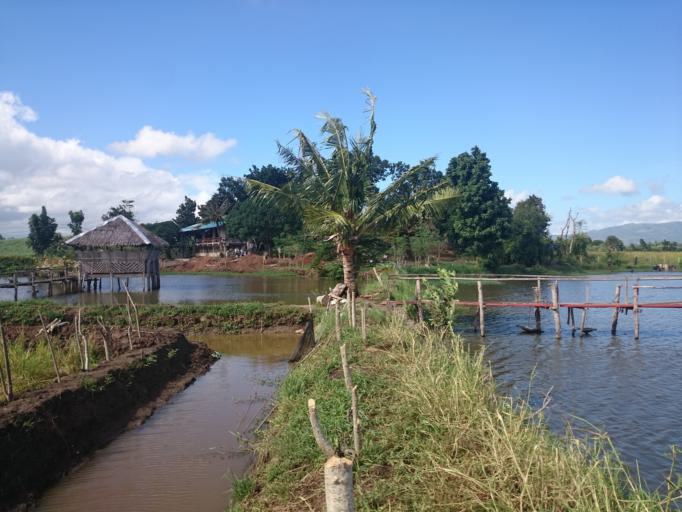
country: PH
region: Central Visayas
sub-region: Province of Negros Oriental
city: Tanjay
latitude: 9.5005
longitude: 123.1548
